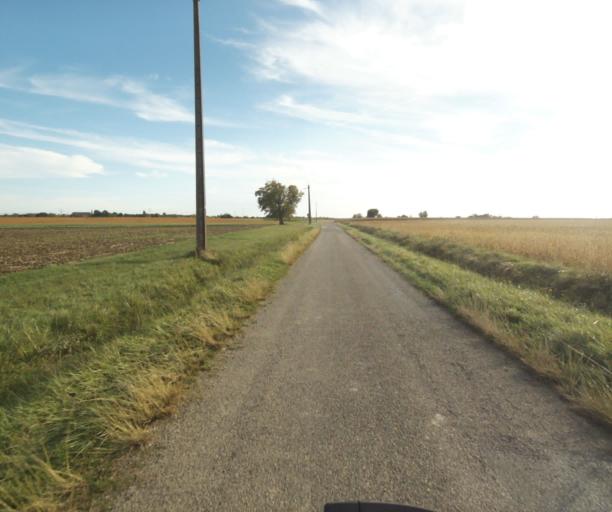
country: FR
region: Midi-Pyrenees
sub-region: Departement du Tarn-et-Garonne
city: Finhan
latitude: 43.9093
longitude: 1.1298
